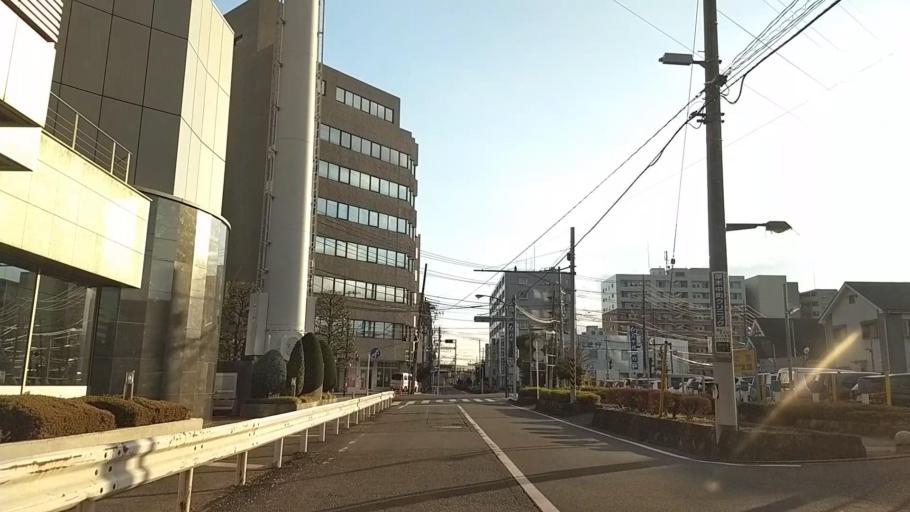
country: JP
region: Kanagawa
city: Atsugi
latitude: 35.4374
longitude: 139.3603
